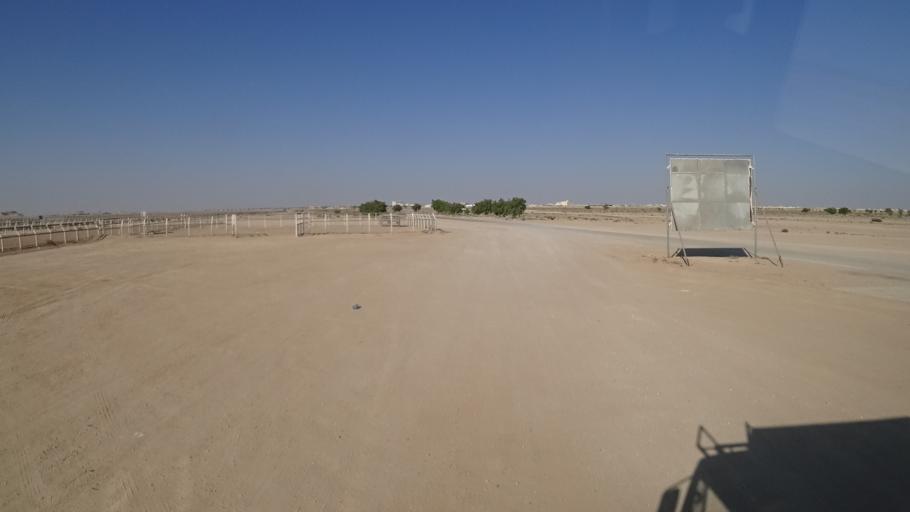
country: OM
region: Zufar
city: Salalah
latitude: 17.5942
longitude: 54.0259
